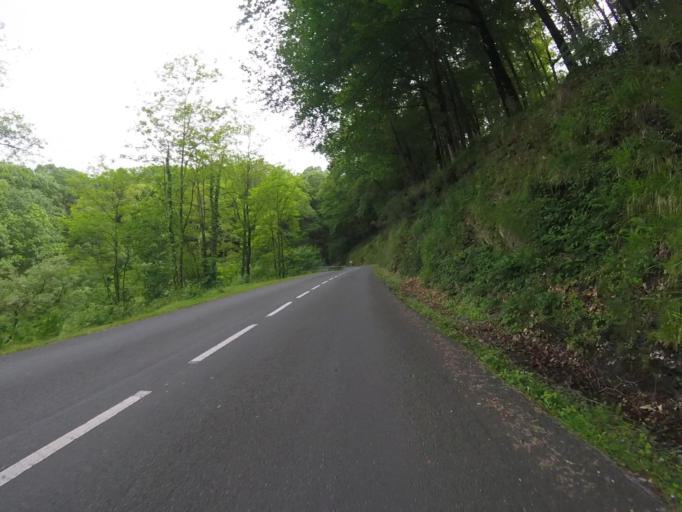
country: ES
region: Navarre
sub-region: Provincia de Navarra
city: Arano
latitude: 43.2521
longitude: -1.8490
